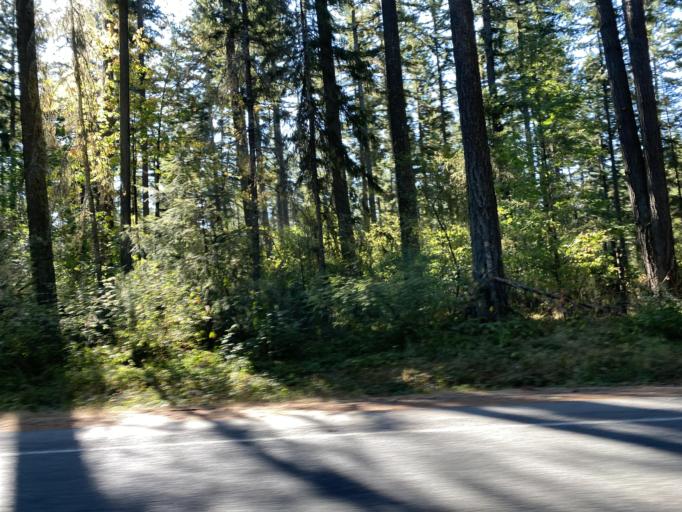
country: US
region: Washington
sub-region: Thurston County
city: Rainier
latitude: 46.9427
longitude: -122.7664
